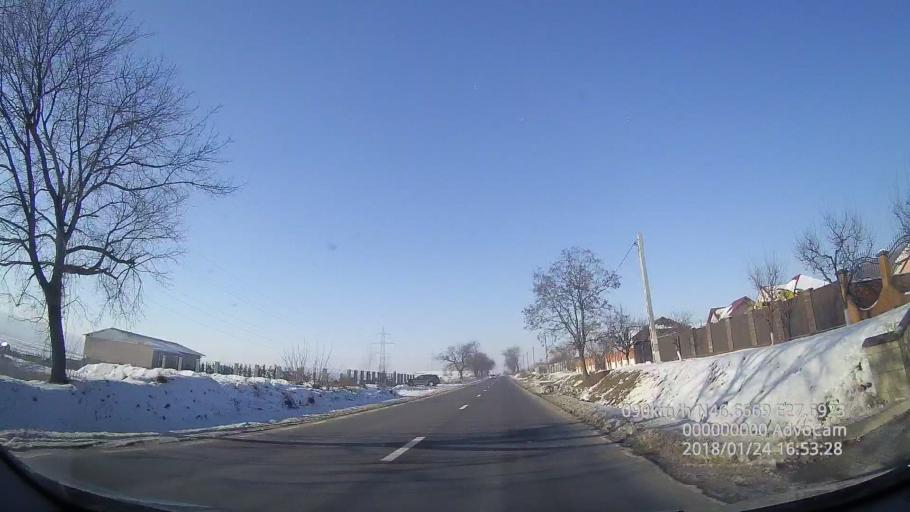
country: RO
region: Vaslui
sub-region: Municipiul Vaslui
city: Brodoc
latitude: 46.6673
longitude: 27.6919
